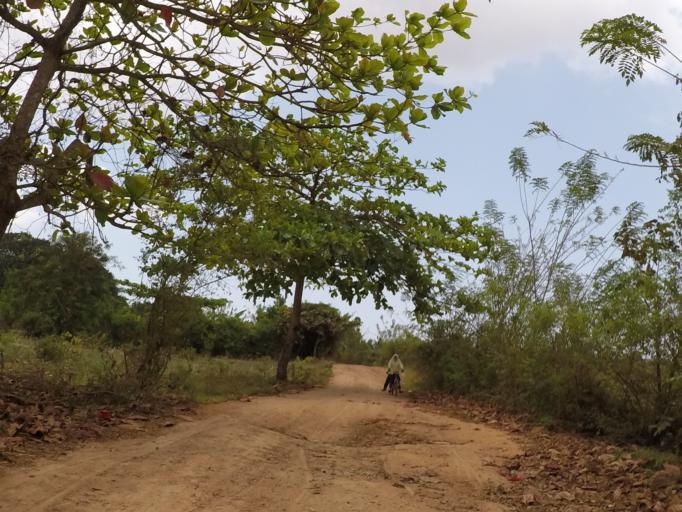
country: TZ
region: Zanzibar Central/South
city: Koani
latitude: -6.1814
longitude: 39.3120
